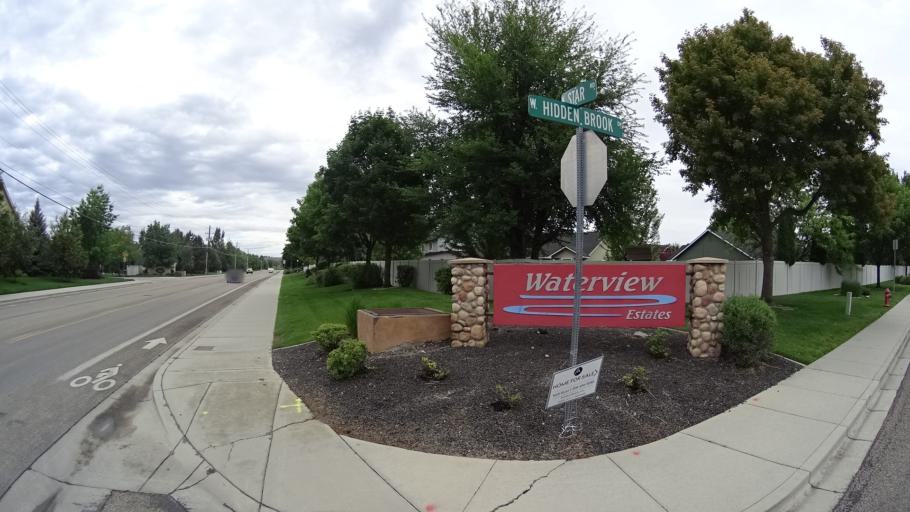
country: US
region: Idaho
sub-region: Ada County
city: Star
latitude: 43.7013
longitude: -116.4932
